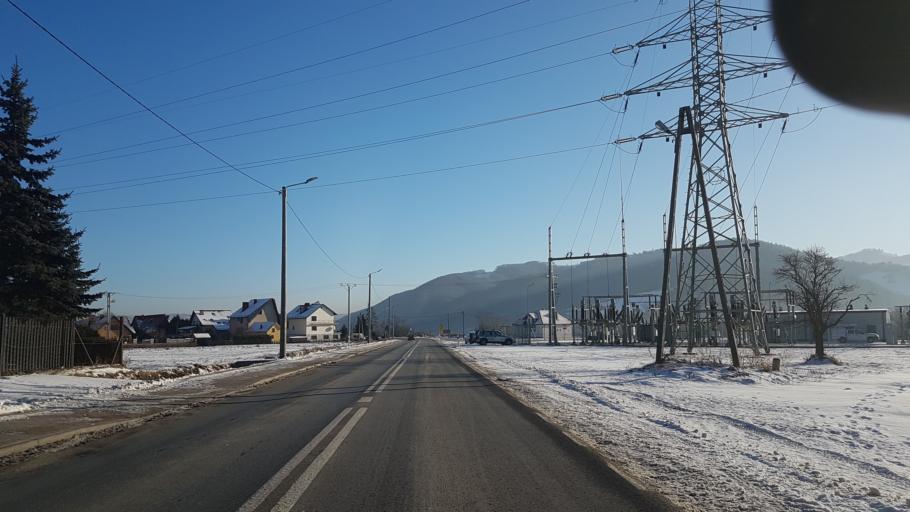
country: PL
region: Lesser Poland Voivodeship
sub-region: Powiat nowosadecki
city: Lacko
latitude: 49.5436
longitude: 20.3946
